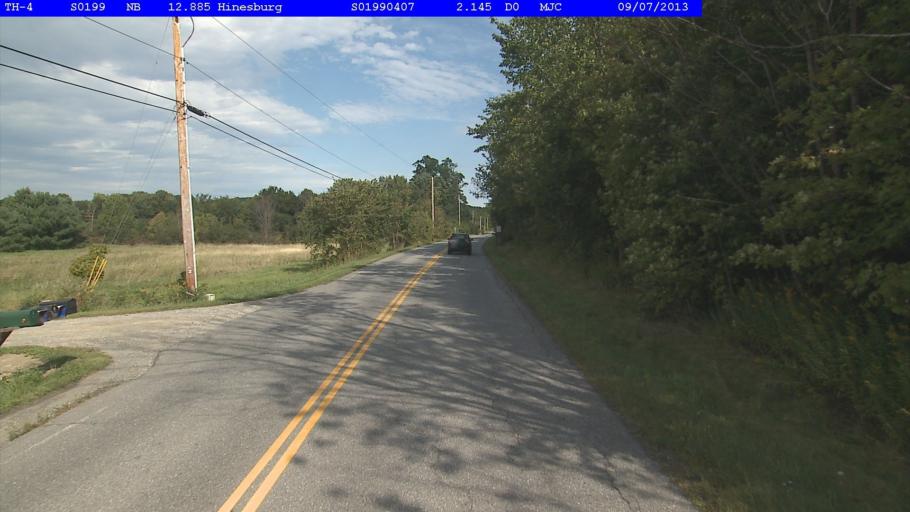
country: US
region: Vermont
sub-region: Chittenden County
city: Hinesburg
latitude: 44.3088
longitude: -73.1091
